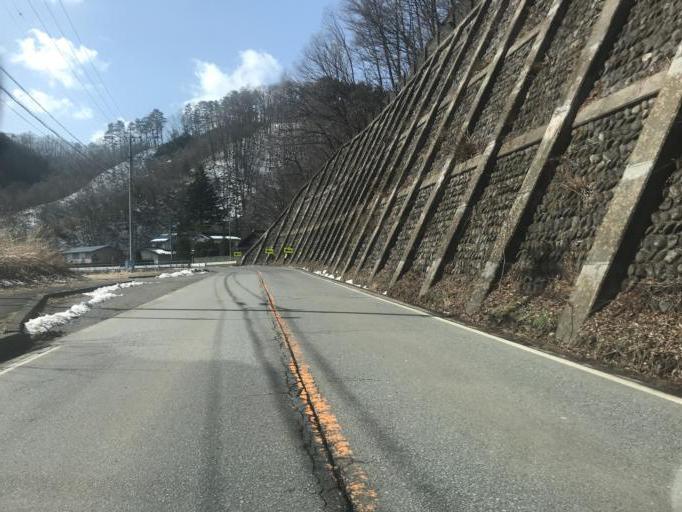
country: JP
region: Nagano
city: Saku
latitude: 36.0148
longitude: 138.4904
